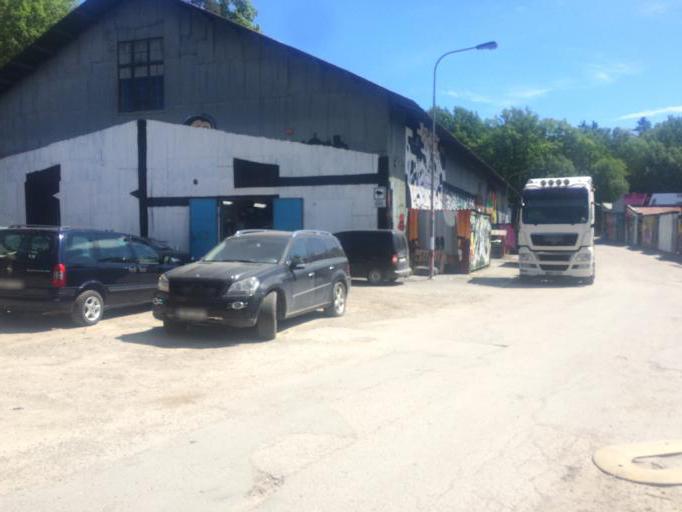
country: SE
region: Stockholm
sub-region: Stockholms Kommun
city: Arsta
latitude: 59.2485
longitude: 18.0429
